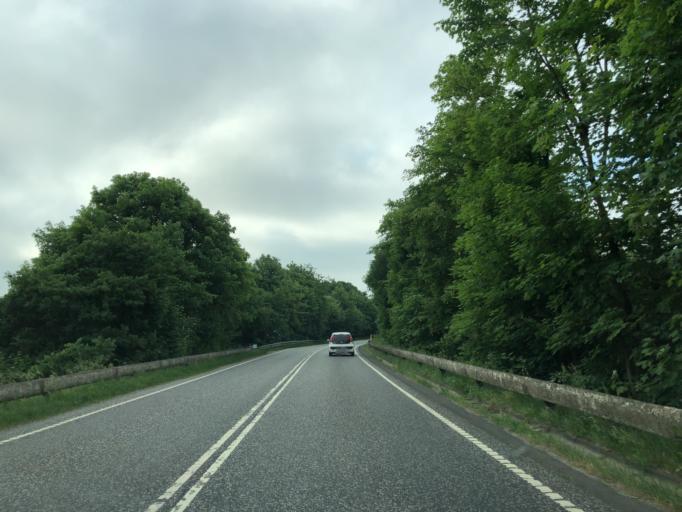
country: DK
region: South Denmark
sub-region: Vejle Kommune
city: Give
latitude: 55.7704
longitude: 9.2879
